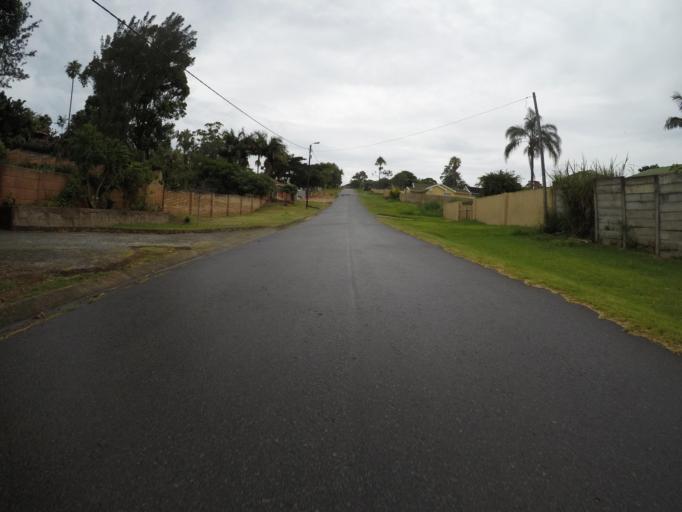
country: ZA
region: Eastern Cape
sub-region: Buffalo City Metropolitan Municipality
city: East London
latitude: -32.9646
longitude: 27.8465
